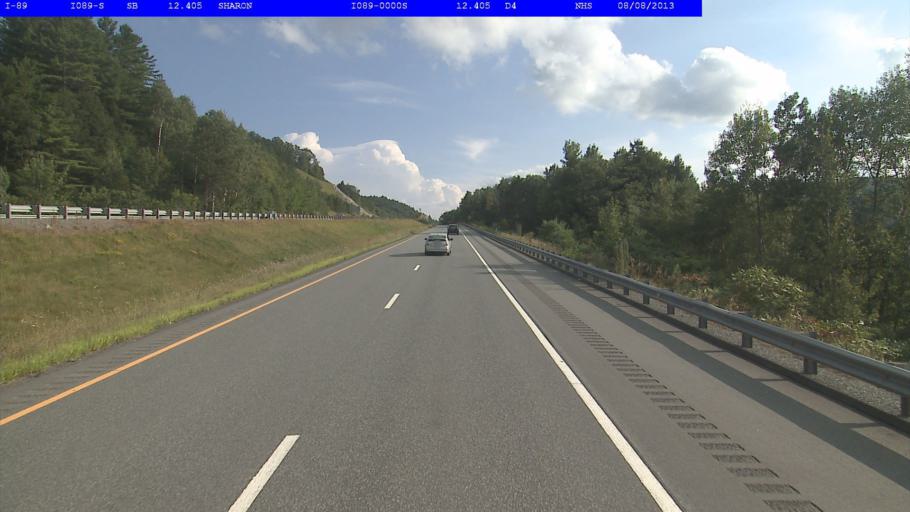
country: US
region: Vermont
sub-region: Windsor County
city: Woodstock
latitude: 43.7740
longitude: -72.4450
